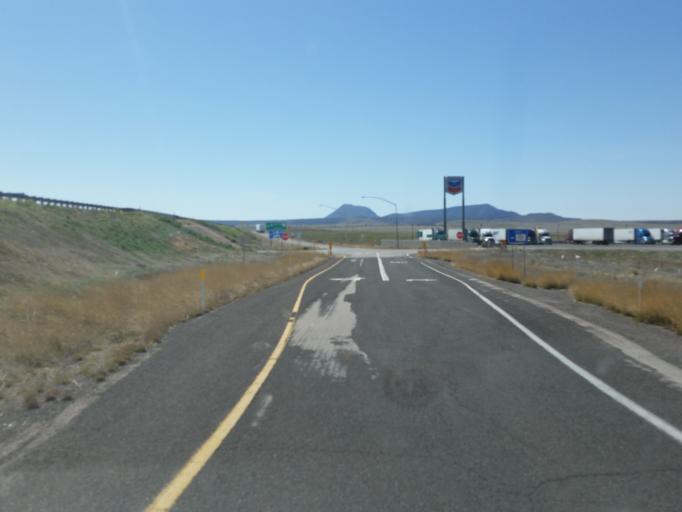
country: US
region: Arizona
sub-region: Yavapai County
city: Paulden
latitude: 35.3106
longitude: -112.8571
